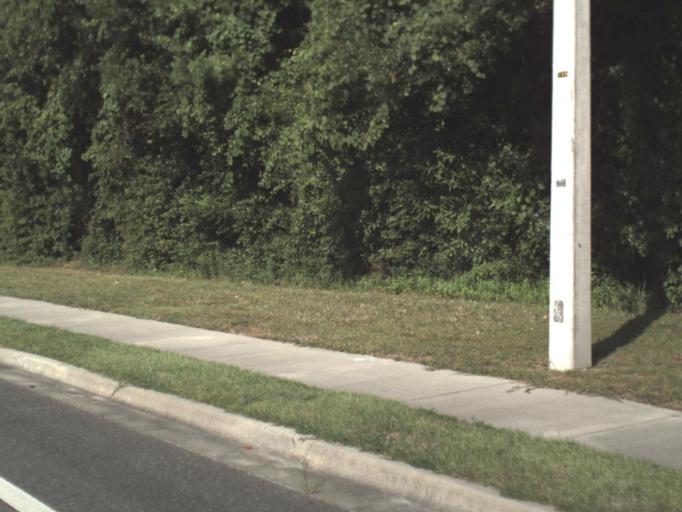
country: US
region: Florida
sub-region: Columbia County
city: Lake City
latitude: 30.1619
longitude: -82.6449
